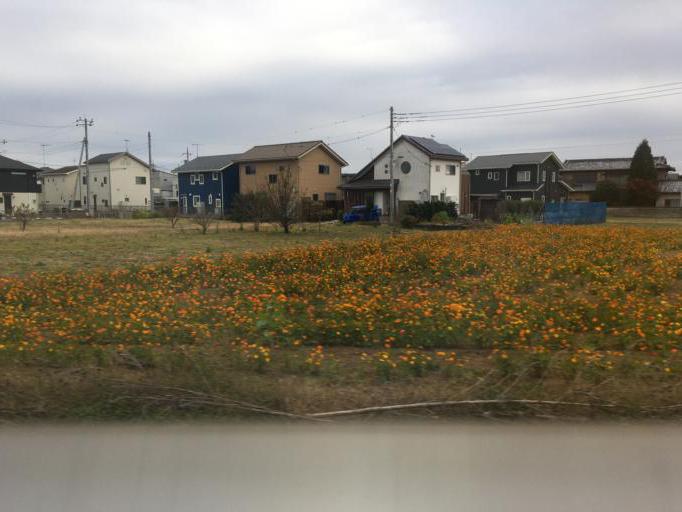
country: JP
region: Tochigi
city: Tochigi
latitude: 36.3422
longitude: 139.6914
